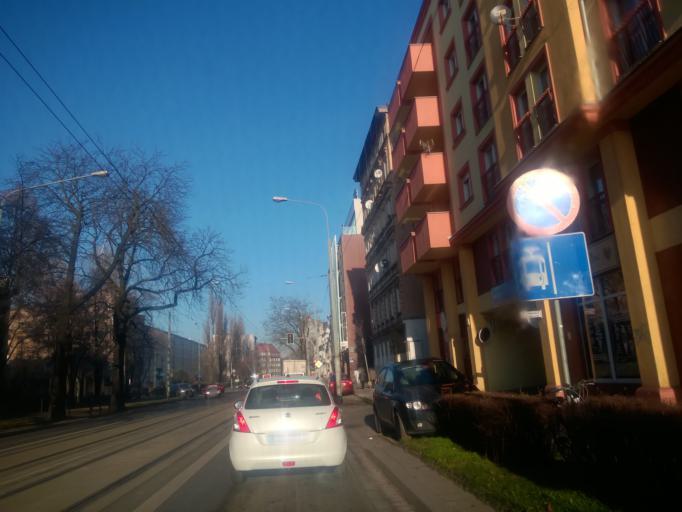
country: PL
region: Lower Silesian Voivodeship
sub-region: Powiat wroclawski
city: Wroclaw
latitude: 51.0904
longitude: 17.0446
